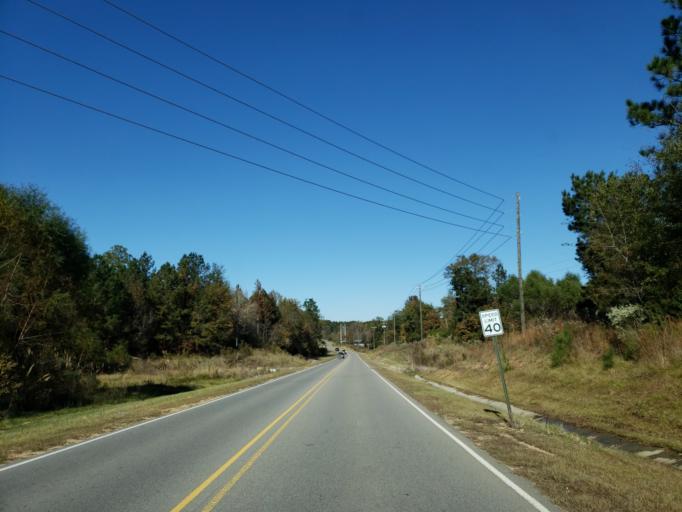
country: US
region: Mississippi
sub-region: Lamar County
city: Arnold Line
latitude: 31.3301
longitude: -89.3996
